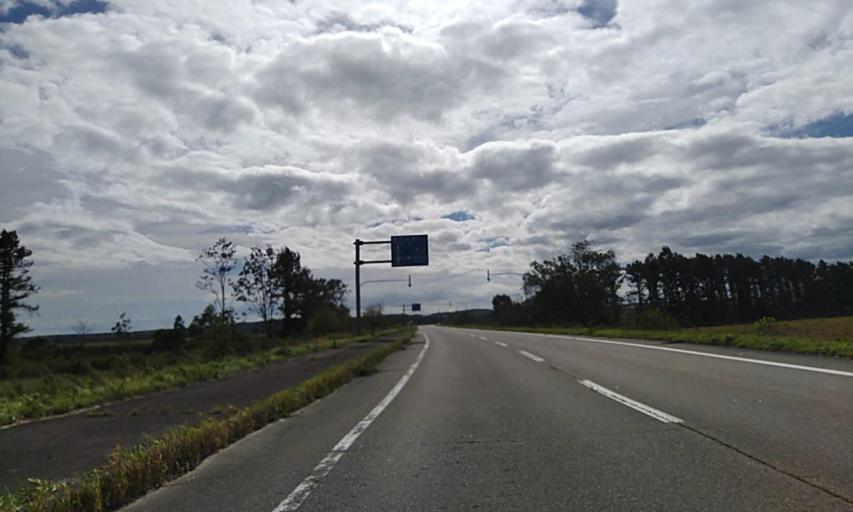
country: JP
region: Hokkaido
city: Obihiro
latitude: 42.7161
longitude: 143.6401
